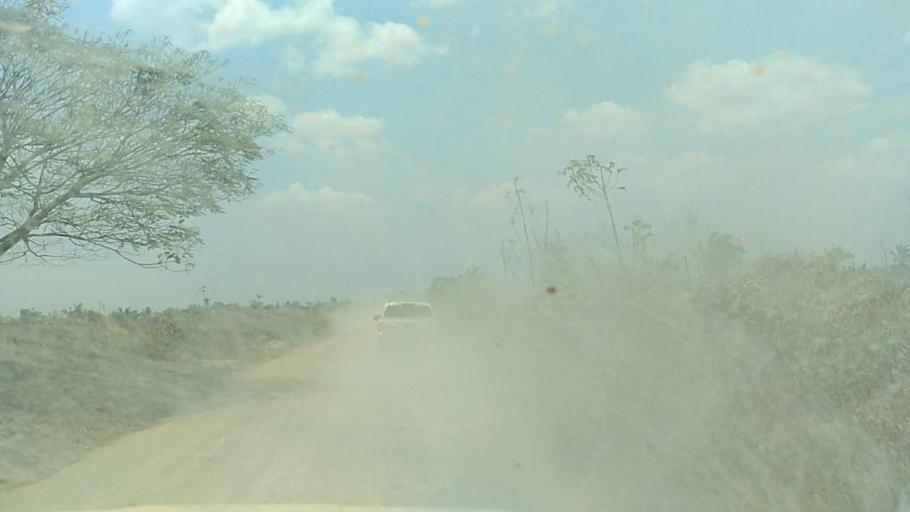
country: BR
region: Rondonia
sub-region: Porto Velho
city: Porto Velho
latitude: -8.7292
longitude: -63.2933
